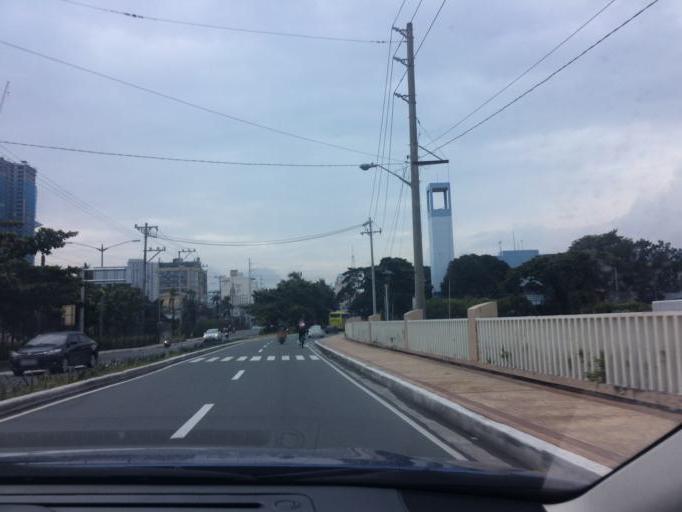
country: PH
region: Metro Manila
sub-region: City of Manila
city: Port Area
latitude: 14.5515
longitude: 120.9869
